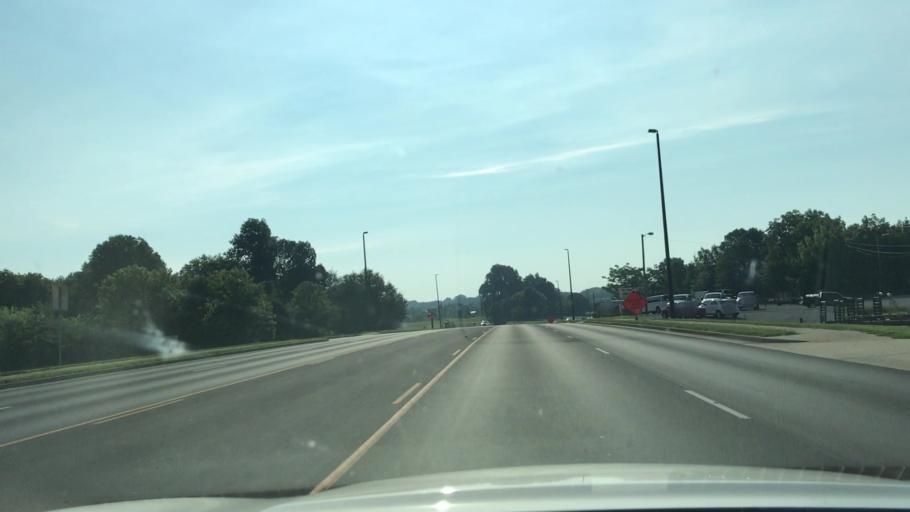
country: US
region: Kentucky
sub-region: Barren County
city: Glasgow
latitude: 37.0100
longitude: -85.9444
